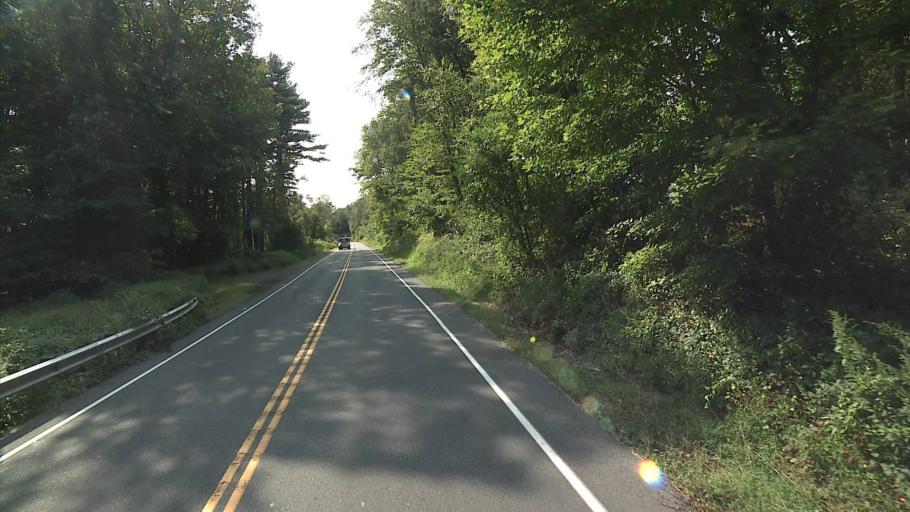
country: US
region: Connecticut
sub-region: Fairfield County
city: Southport
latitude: 41.2254
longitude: -73.3138
